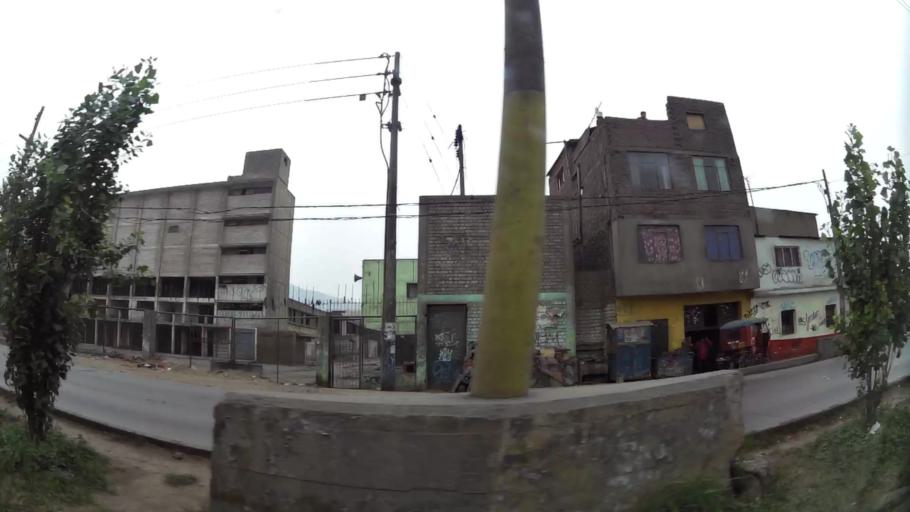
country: PE
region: Lima
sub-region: Lima
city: Santa Maria
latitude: -12.0217
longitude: -76.9069
